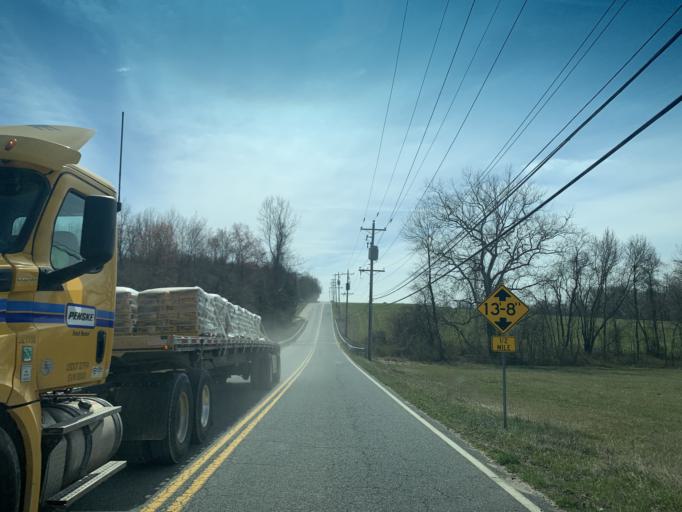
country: US
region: Maryland
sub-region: Cecil County
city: Perryville
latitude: 39.5789
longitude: -76.0266
